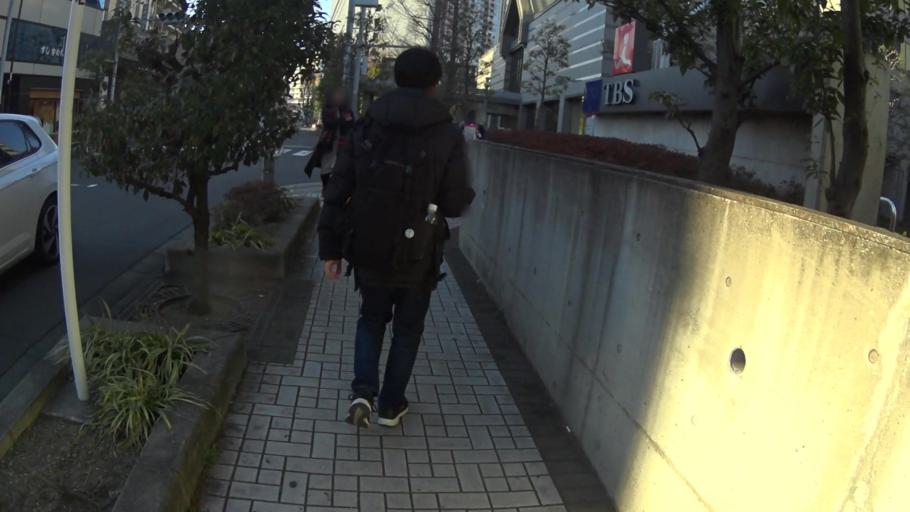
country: JP
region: Tokyo
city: Tokyo
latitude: 35.6713
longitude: 139.7336
